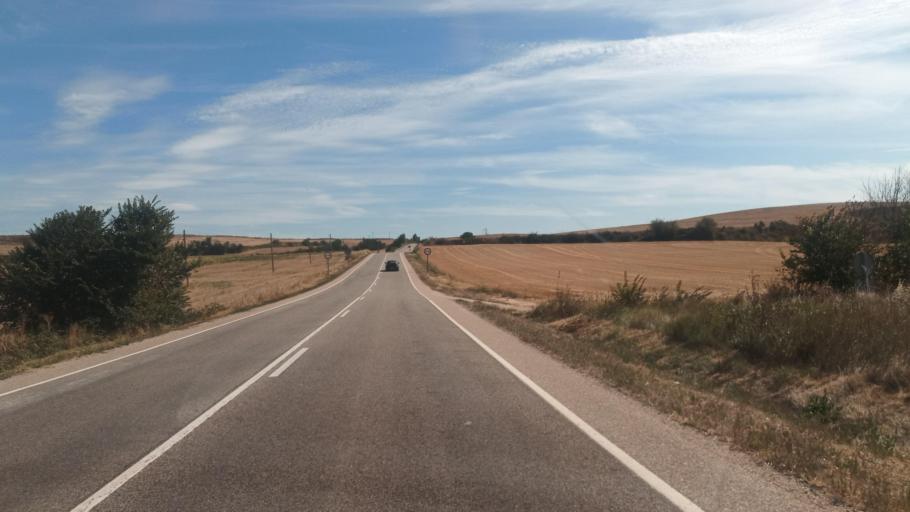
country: ES
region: Castille and Leon
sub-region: Provincia de Burgos
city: Aguilar de Bureba
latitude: 42.5777
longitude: -3.3340
